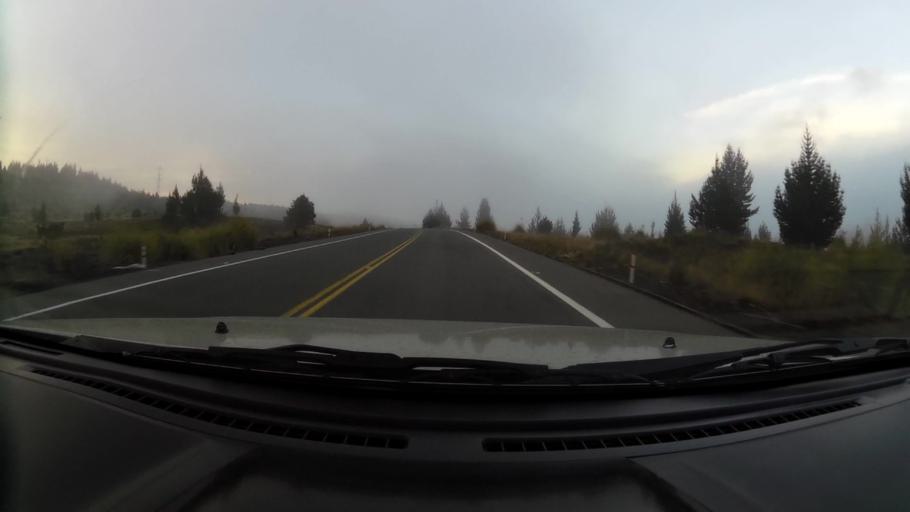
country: EC
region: Chimborazo
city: Alausi
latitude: -2.0545
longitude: -78.7437
